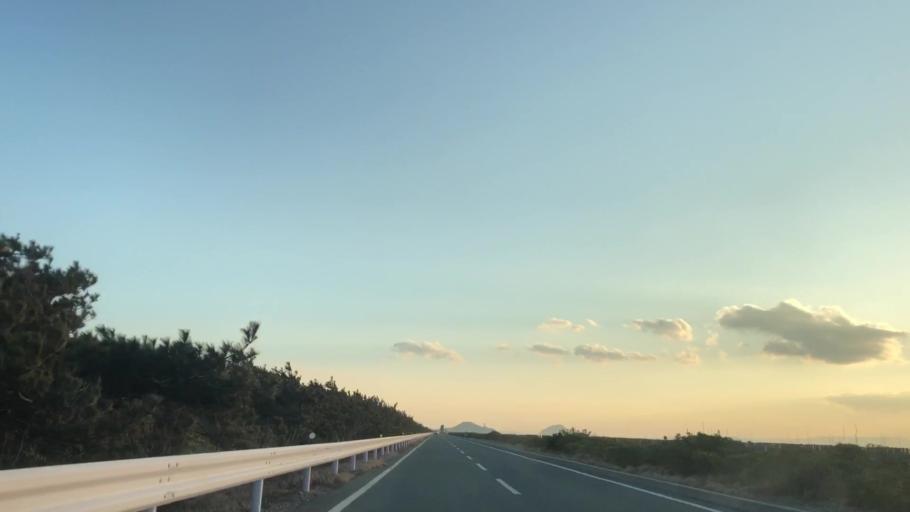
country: JP
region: Aichi
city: Toyohama
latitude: 34.6345
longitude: 137.0503
